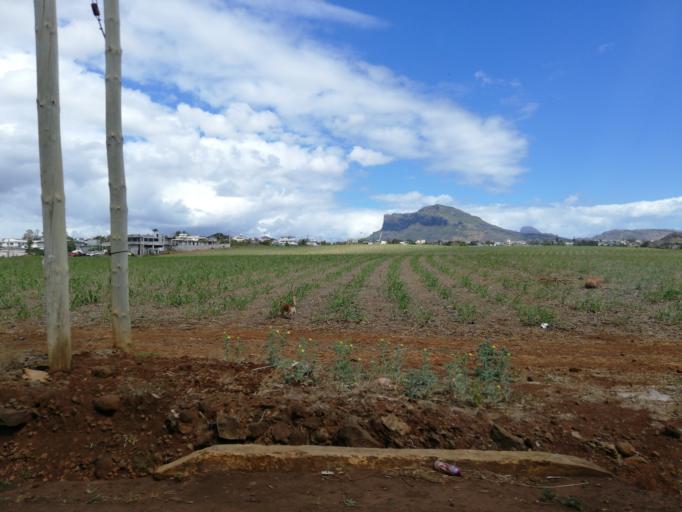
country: MU
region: Black River
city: Petite Riviere
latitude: -20.2145
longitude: 57.4595
